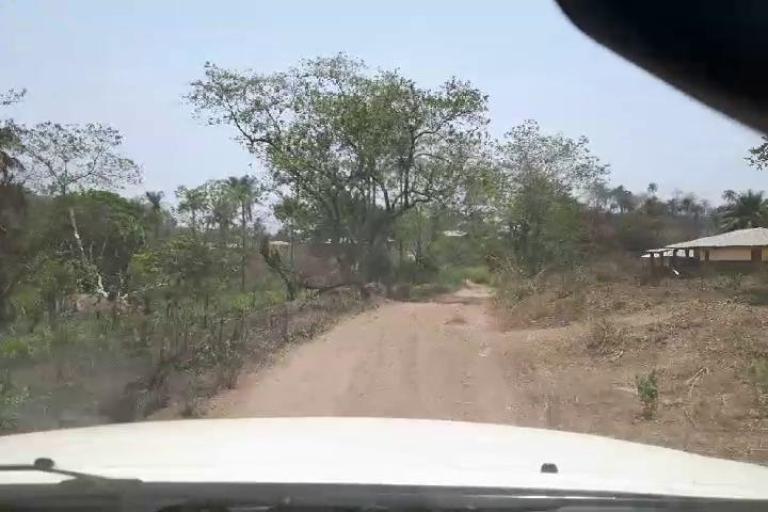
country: SL
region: Northern Province
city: Alikalia
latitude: 9.0664
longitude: -11.4842
